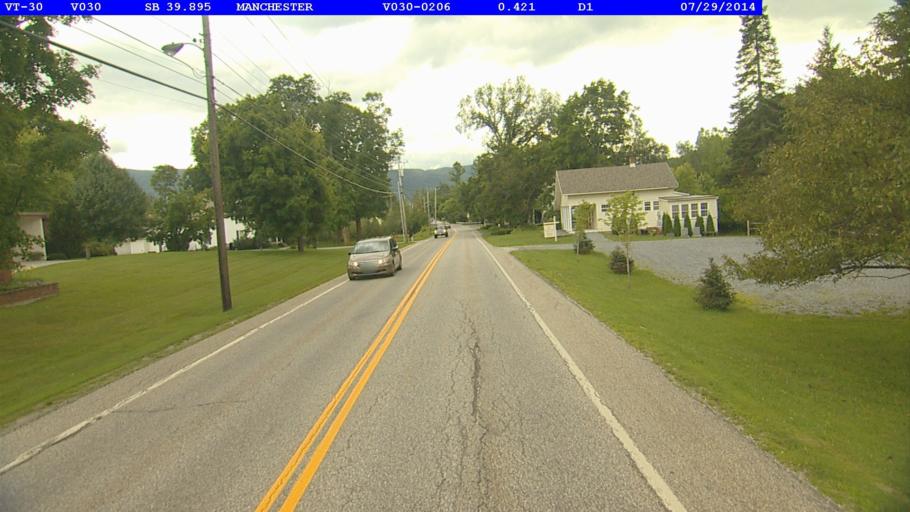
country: US
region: Vermont
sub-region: Bennington County
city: Manchester Center
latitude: 43.1828
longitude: -73.0580
